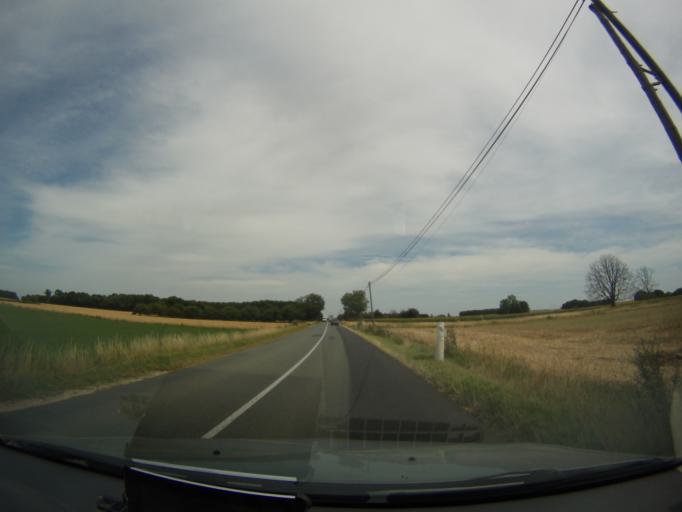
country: FR
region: Poitou-Charentes
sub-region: Departement de la Vienne
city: Mirebeau
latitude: 46.7566
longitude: 0.1629
